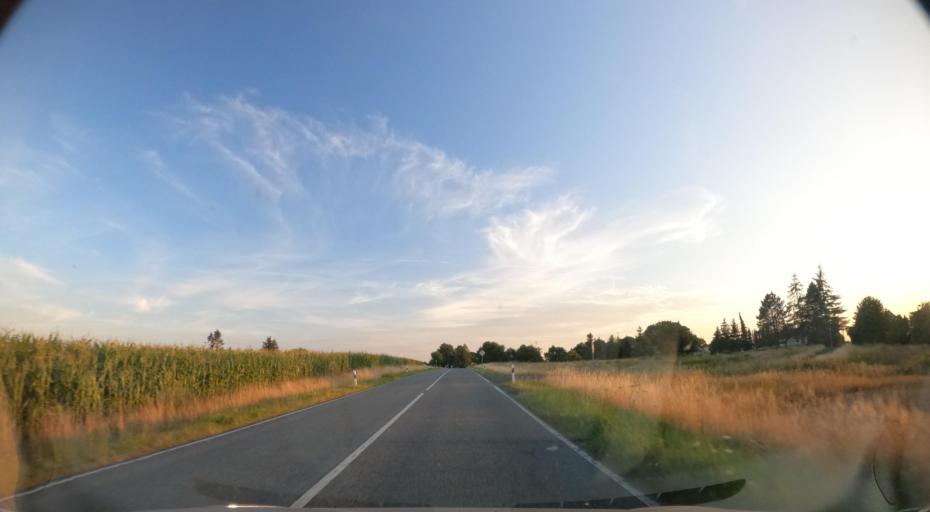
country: DE
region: Mecklenburg-Vorpommern
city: Strasburg
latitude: 53.4831
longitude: 13.6724
